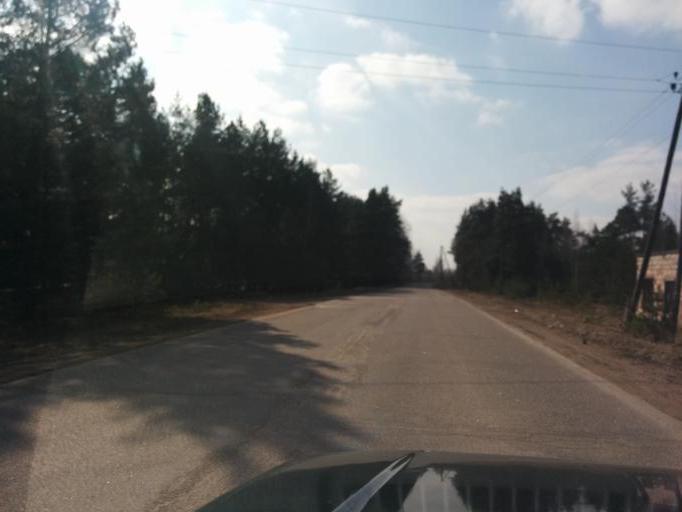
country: LV
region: Kekava
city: Kekava
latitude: 56.8493
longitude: 24.2595
